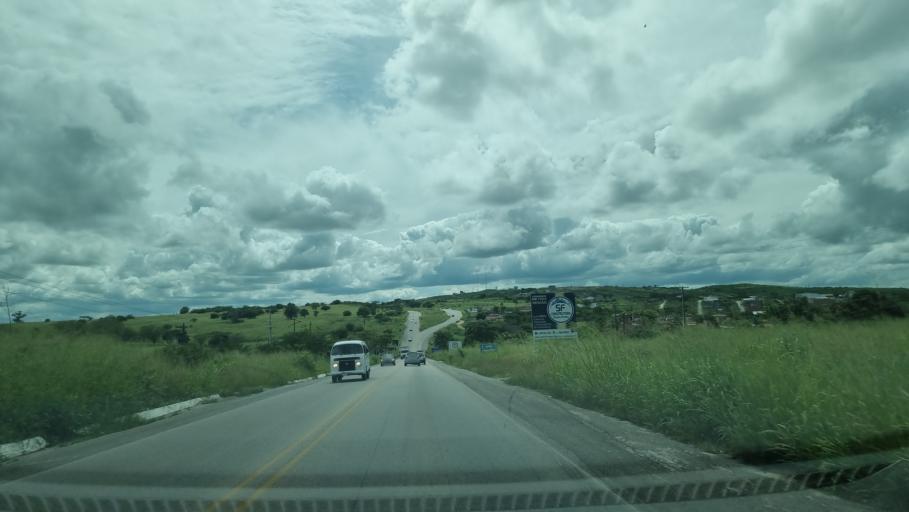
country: BR
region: Pernambuco
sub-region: Caruaru
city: Caruaru
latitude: -8.3352
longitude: -35.9806
